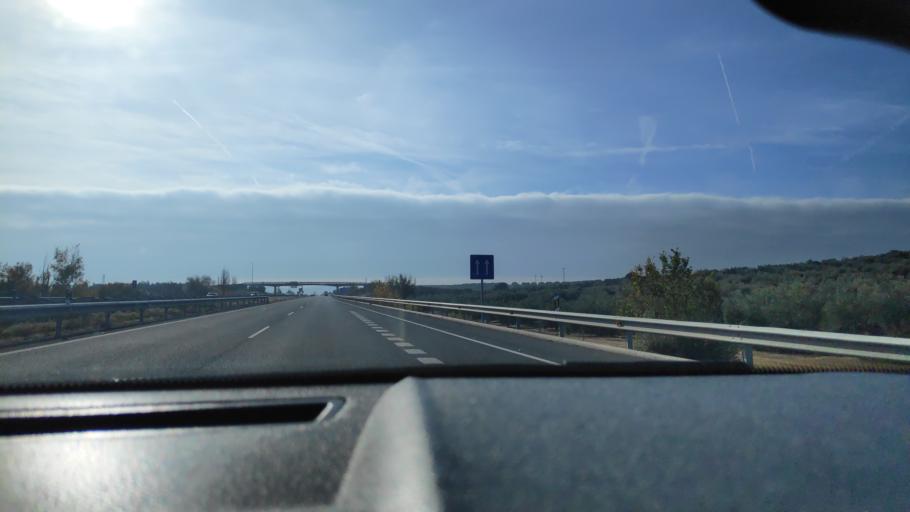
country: ES
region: Andalusia
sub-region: Provincia de Jaen
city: Bailen
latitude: 38.0936
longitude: -3.7391
